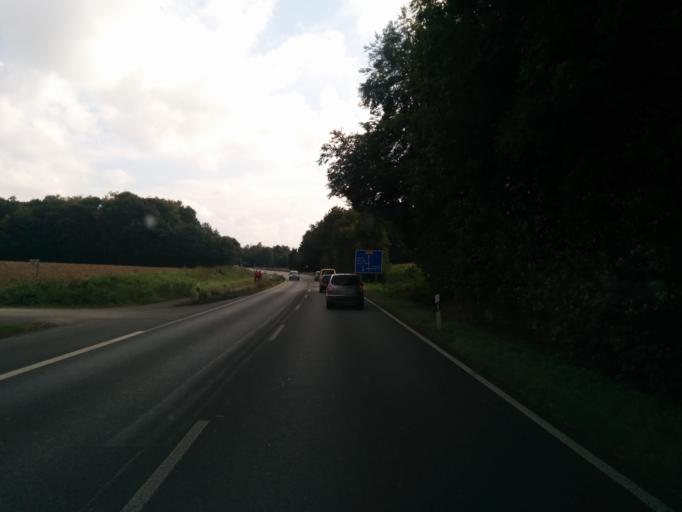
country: DE
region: North Rhine-Westphalia
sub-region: Regierungsbezirk Munster
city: Dulmen
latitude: 51.8477
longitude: 7.2525
